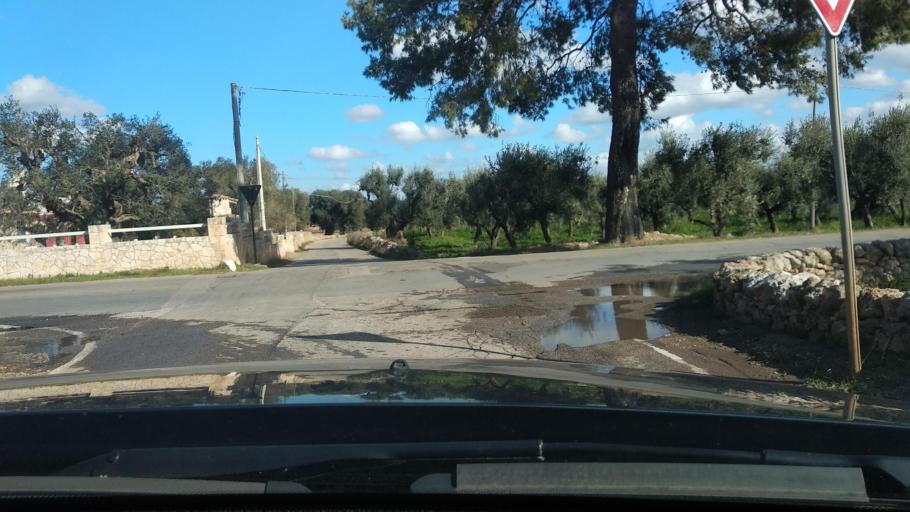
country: IT
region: Apulia
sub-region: Provincia di Brindisi
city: Fasano
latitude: 40.8286
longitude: 17.3771
